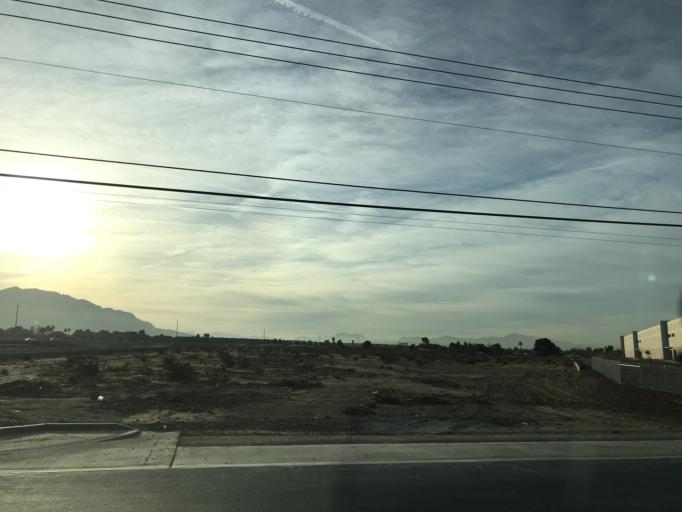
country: US
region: Nevada
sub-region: Clark County
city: Sunrise Manor
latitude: 36.2285
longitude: -115.0749
